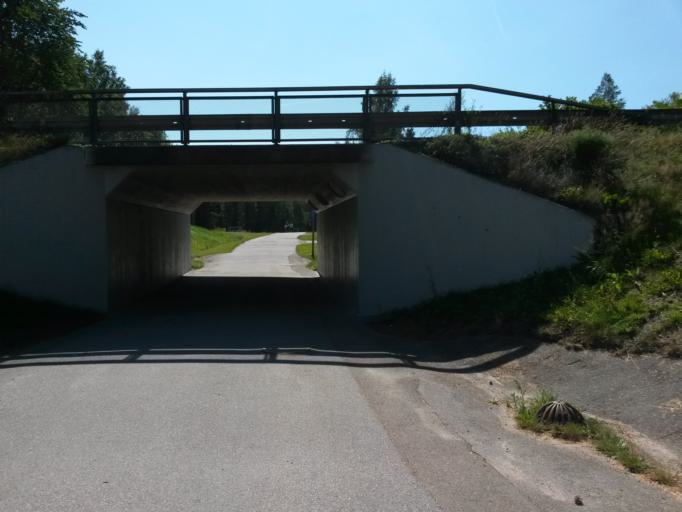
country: SE
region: Vaestra Goetaland
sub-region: Lidkopings Kommun
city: Lidkoping
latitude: 58.4889
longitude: 13.1535
